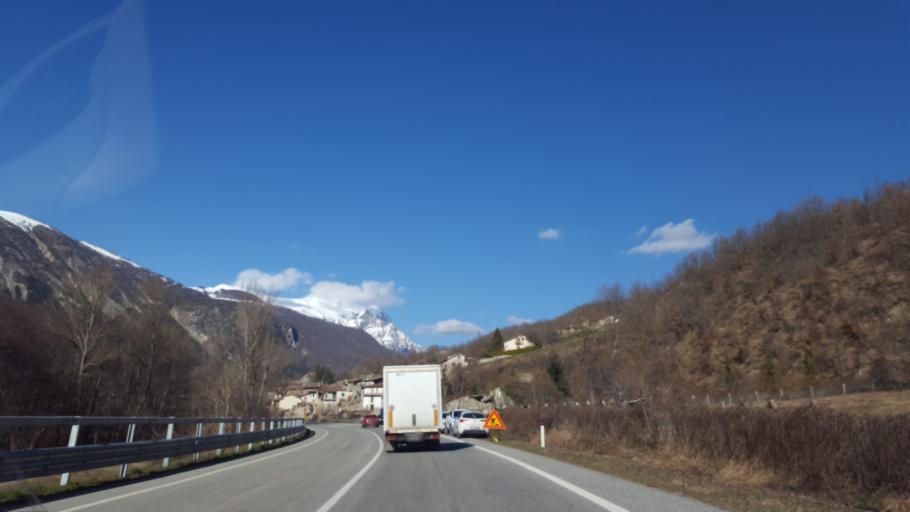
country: IT
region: Latium
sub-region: Provincia di Rieti
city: Accumoli
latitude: 42.7303
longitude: 13.2694
